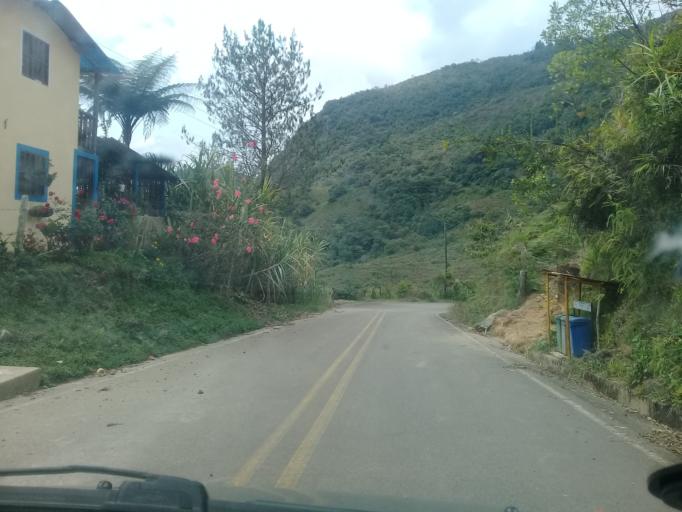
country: CO
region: Cundinamarca
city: Gachala
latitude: 4.7034
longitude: -73.4586
